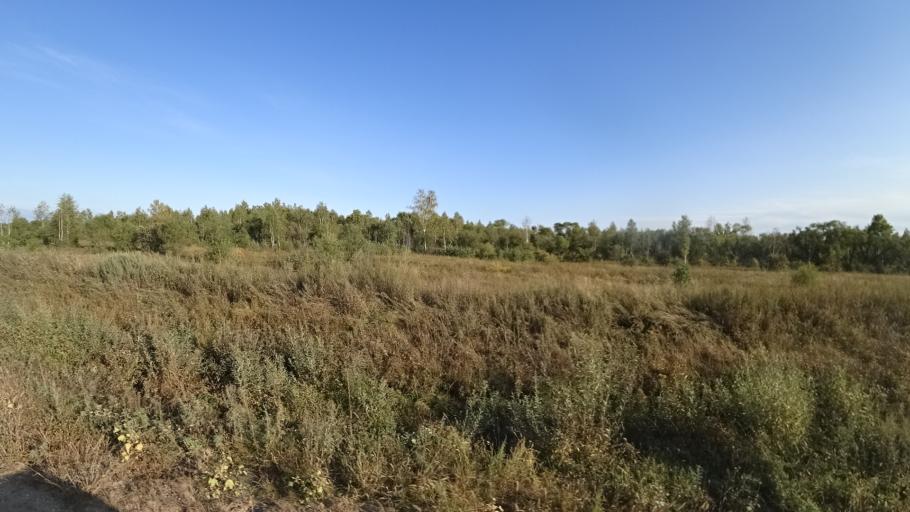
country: RU
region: Amur
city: Arkhara
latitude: 49.3488
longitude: 130.1266
